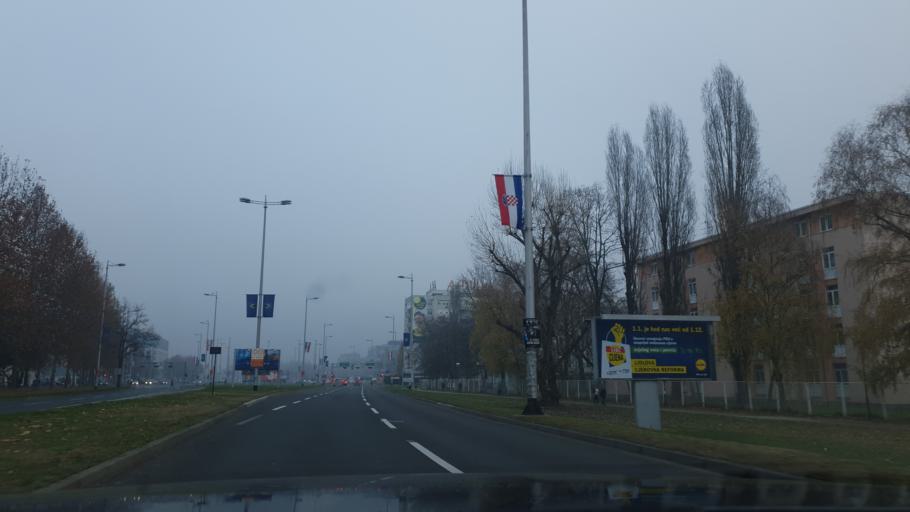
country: HR
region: Grad Zagreb
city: Novi Zagreb
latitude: 45.7739
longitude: 15.9804
